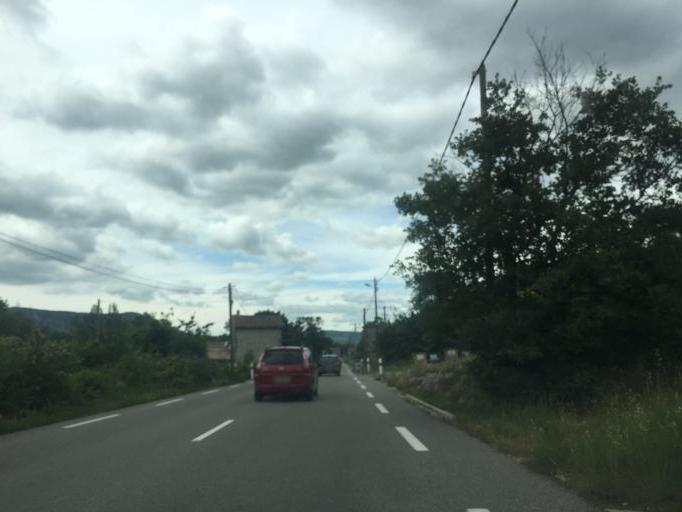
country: FR
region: Rhone-Alpes
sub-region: Departement de l'Ardeche
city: Alba-la-Romaine
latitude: 44.5470
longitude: 4.6108
